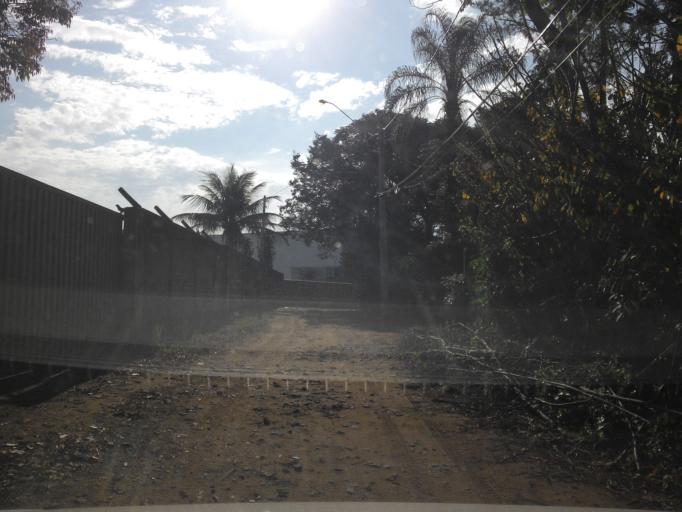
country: BR
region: Sao Paulo
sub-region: Hortolandia
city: Hortolandia
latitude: -22.9046
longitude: -47.2263
